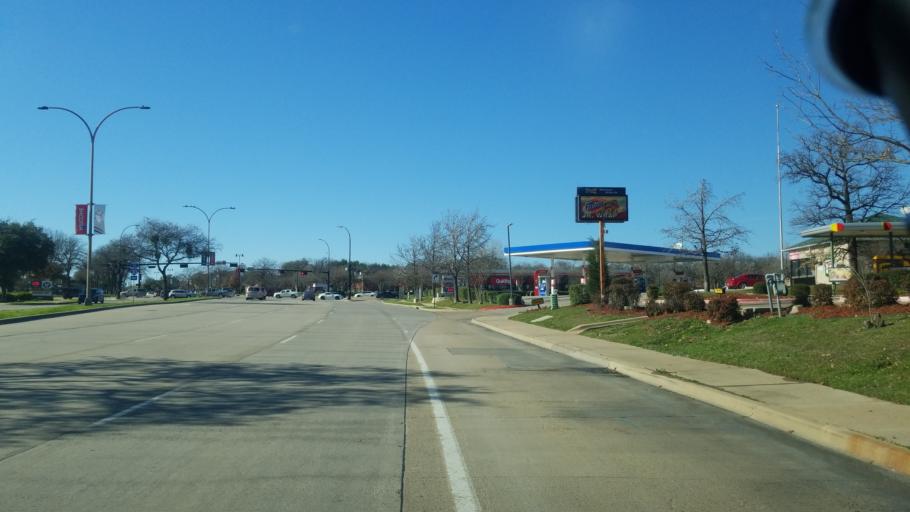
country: US
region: Texas
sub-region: Tarrant County
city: Arlington
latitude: 32.7624
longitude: -97.0740
